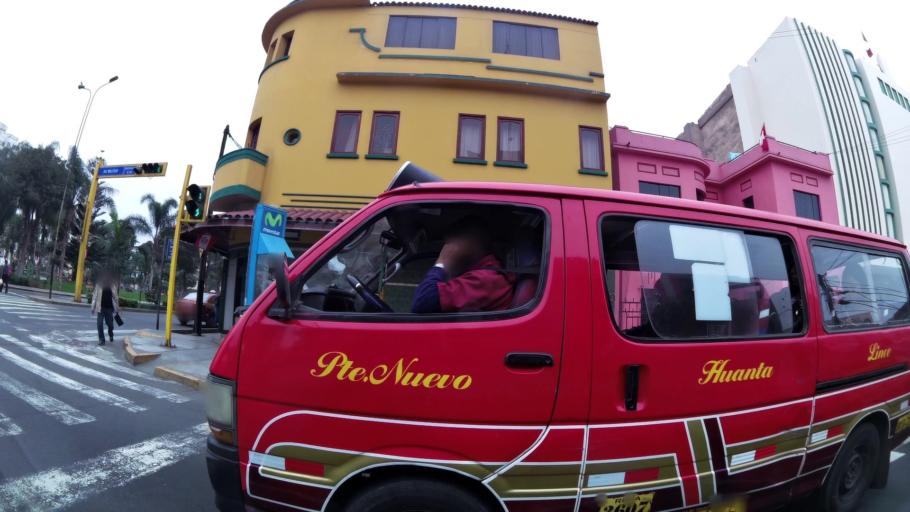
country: PE
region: Lima
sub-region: Lima
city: San Luis
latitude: -12.0833
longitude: -77.0315
